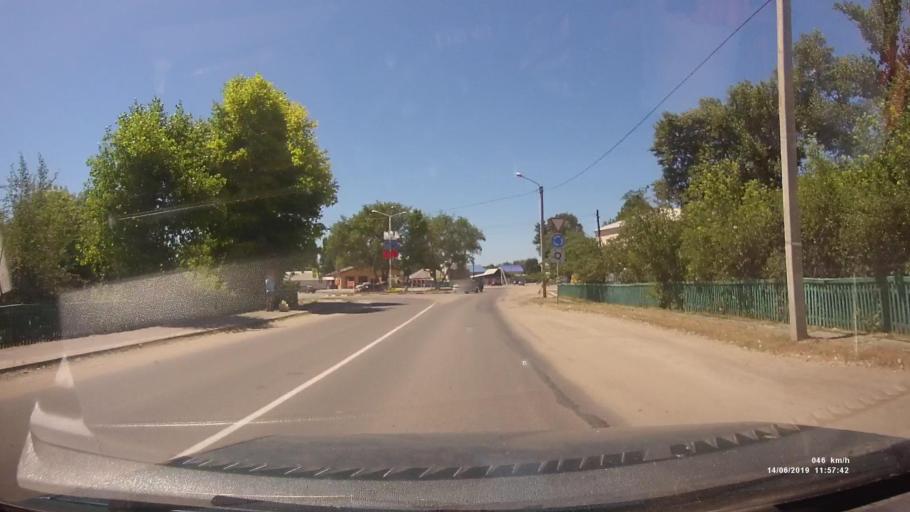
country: RU
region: Rostov
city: Kazanskaya
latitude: 49.7982
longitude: 41.1456
